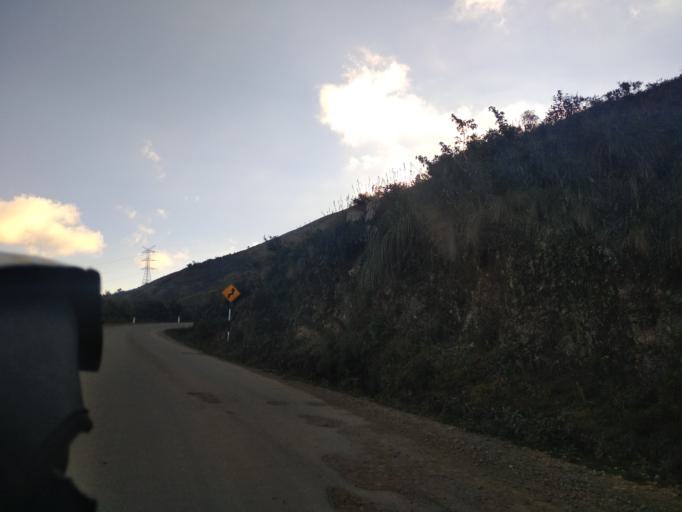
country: PE
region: Amazonas
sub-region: Provincia de Chachapoyas
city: Montevideo
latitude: -6.7146
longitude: -77.8725
